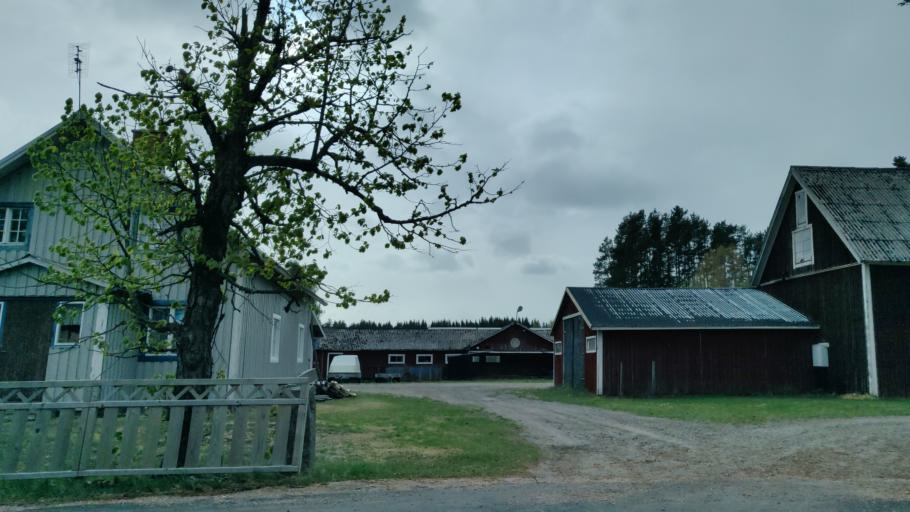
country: SE
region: Vaermland
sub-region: Forshaga Kommun
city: Deje
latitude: 59.6414
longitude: 13.4427
